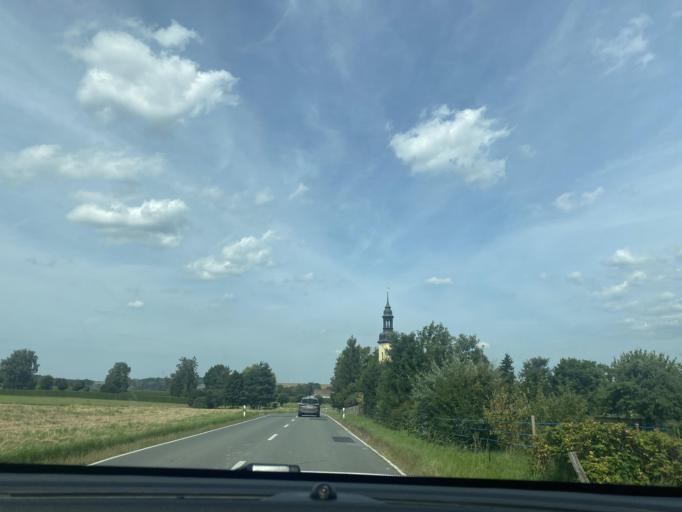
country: DE
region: Saxony
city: Grosshennersdorf
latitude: 50.9882
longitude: 14.7875
